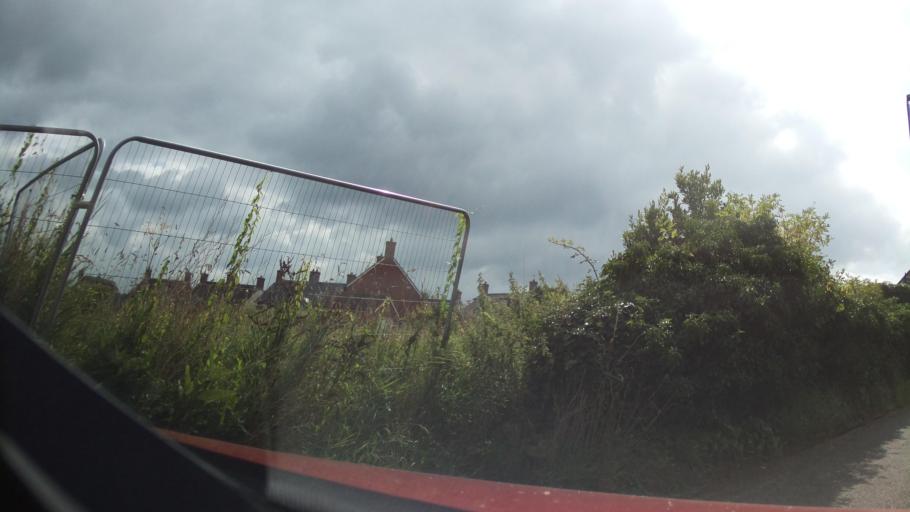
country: GB
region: England
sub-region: Somerset
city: Wincanton
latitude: 51.0051
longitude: -2.4193
